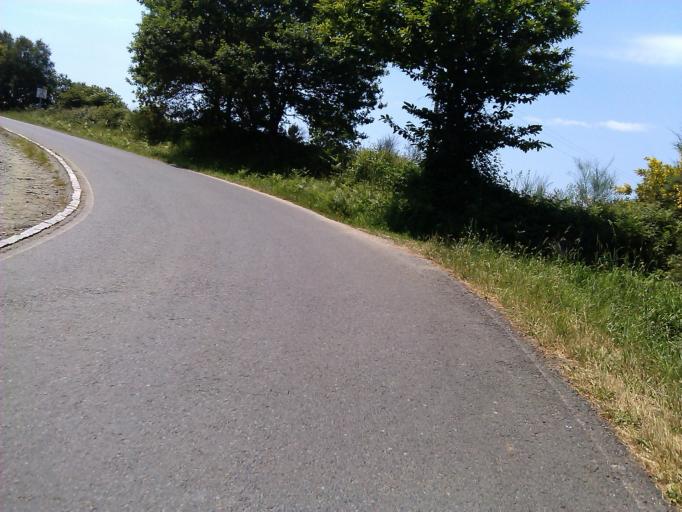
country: ES
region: Galicia
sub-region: Provincia de Lugo
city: Monterroso
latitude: 42.8741
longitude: -7.8179
